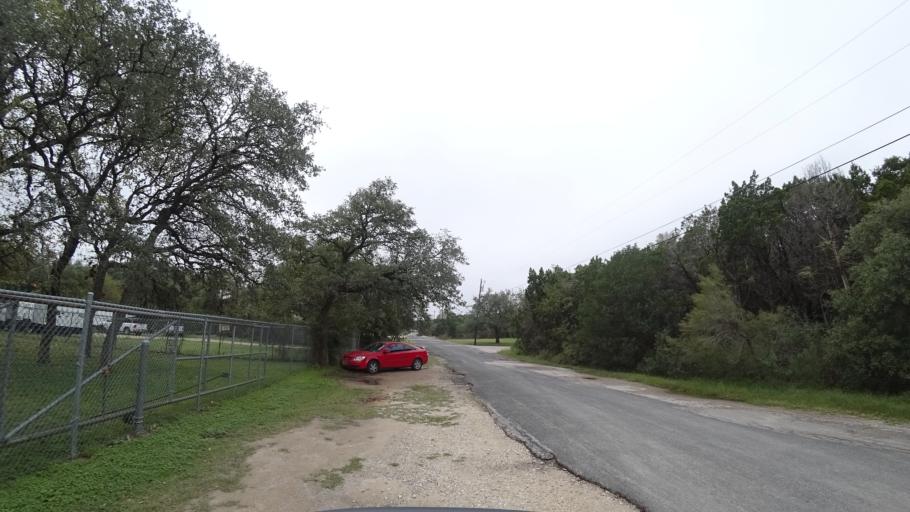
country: US
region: Texas
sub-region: Travis County
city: Barton Creek
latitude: 30.2321
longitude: -97.8943
